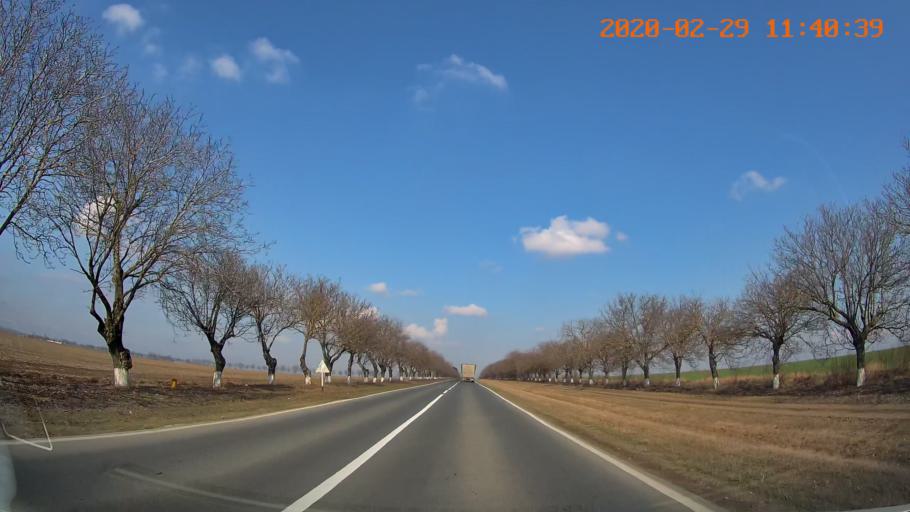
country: MD
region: Rezina
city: Saharna
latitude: 47.6596
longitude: 29.0194
